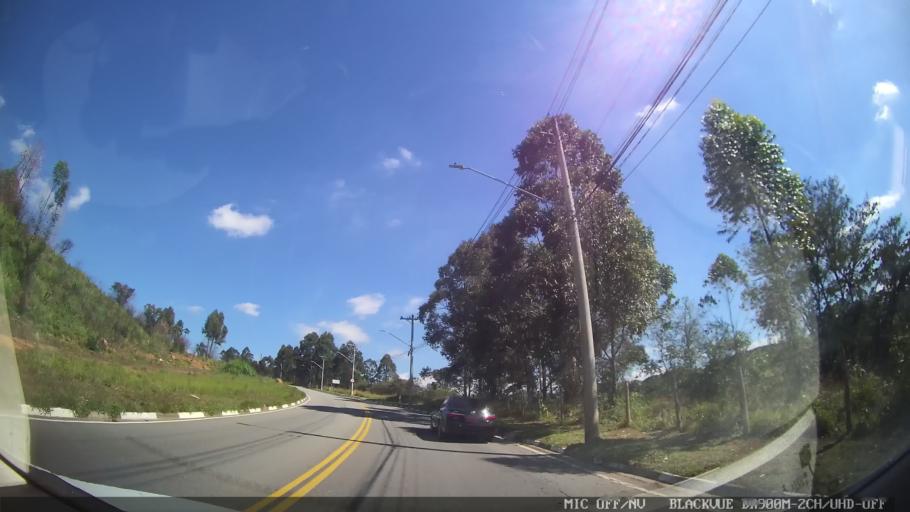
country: BR
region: Sao Paulo
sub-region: Barueri
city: Barueri
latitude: -23.4450
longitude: -46.8359
